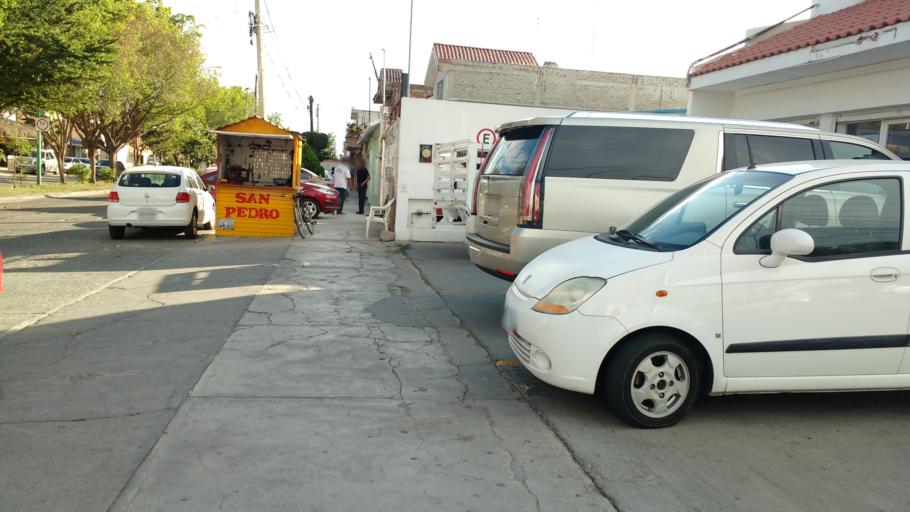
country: MX
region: Guanajuato
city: Leon
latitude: 21.1041
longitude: -101.6458
